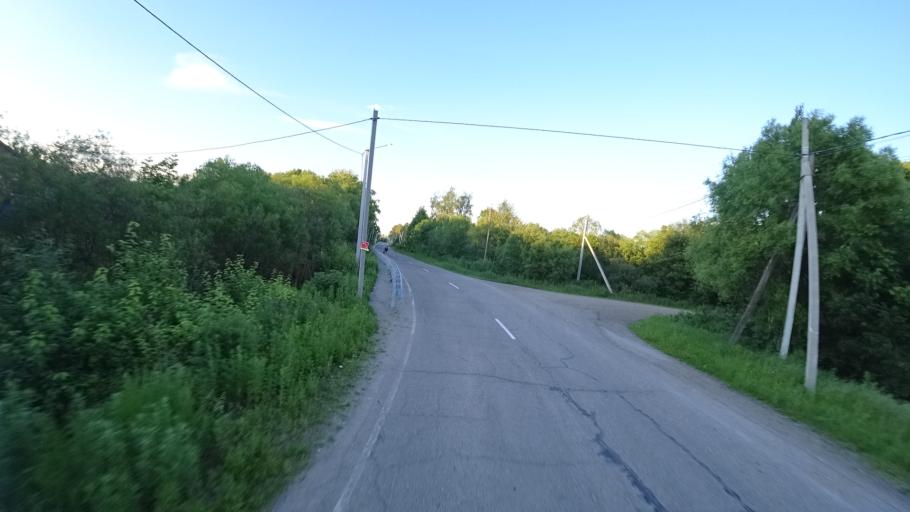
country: RU
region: Khabarovsk Krai
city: Khor
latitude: 47.8531
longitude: 134.9822
